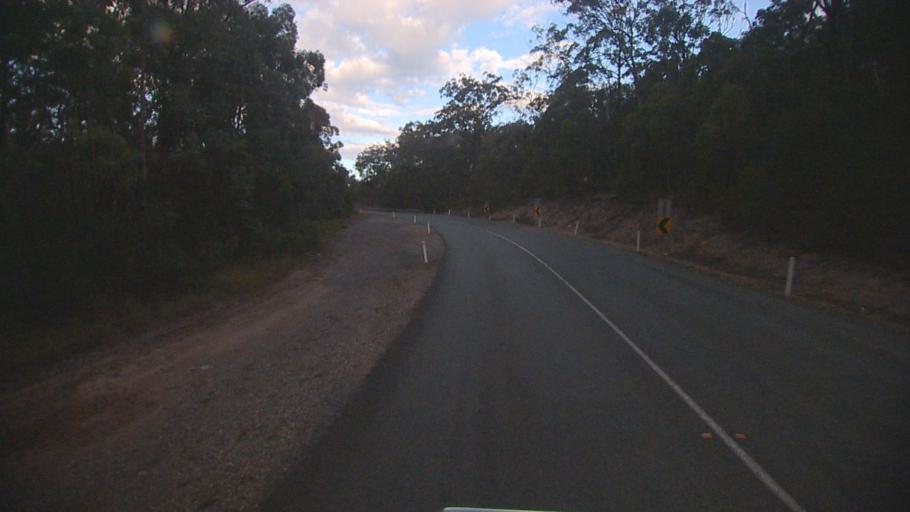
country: AU
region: Queensland
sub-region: Logan
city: Chambers Flat
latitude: -27.8046
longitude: 153.1438
